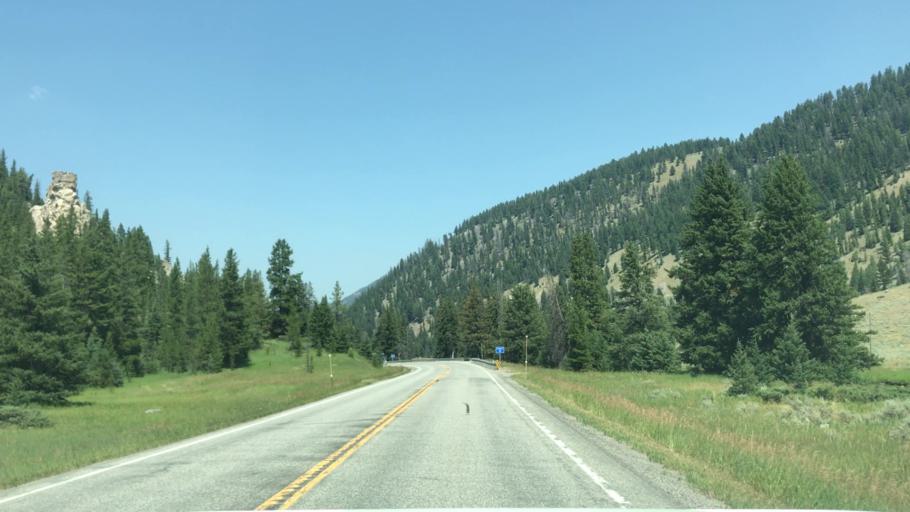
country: US
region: Montana
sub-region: Gallatin County
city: Big Sky
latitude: 45.0814
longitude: -111.2085
